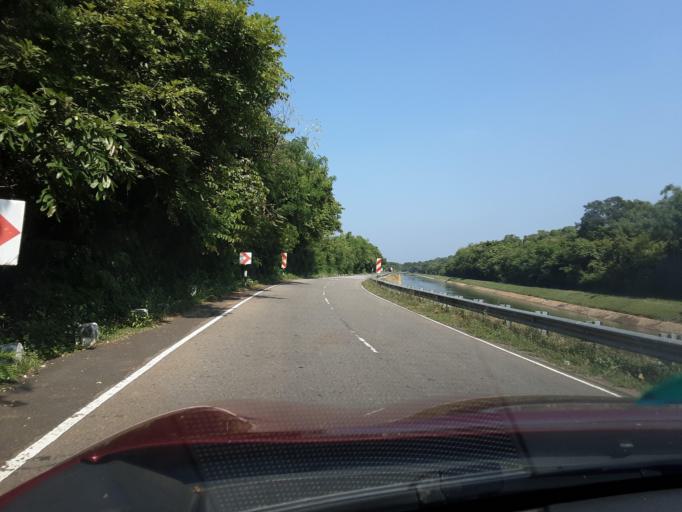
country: LK
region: Uva
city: Badulla
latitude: 7.2758
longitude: 81.0448
